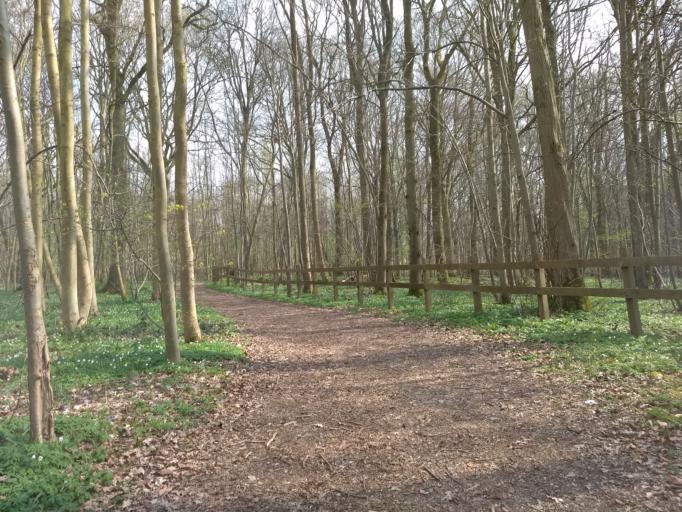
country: FR
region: Nord-Pas-de-Calais
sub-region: Departement du Pas-de-Calais
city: Maroeuil
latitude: 50.3337
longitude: 2.6914
